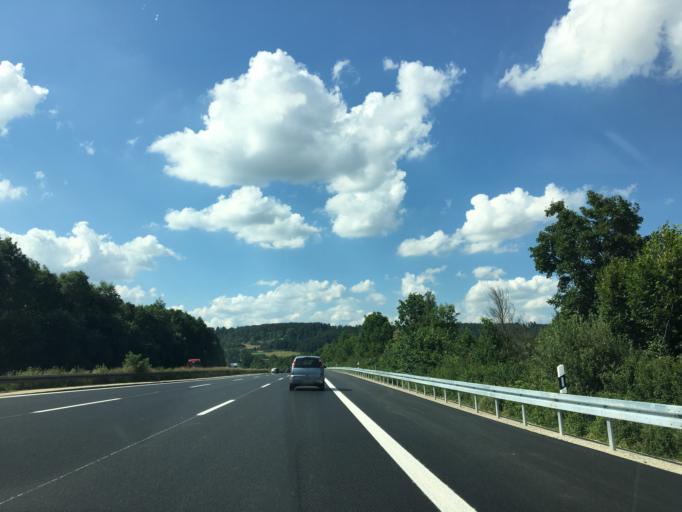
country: DE
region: Bavaria
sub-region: Regierungsbezirk Mittelfranken
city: Greding
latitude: 49.0572
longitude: 11.3263
